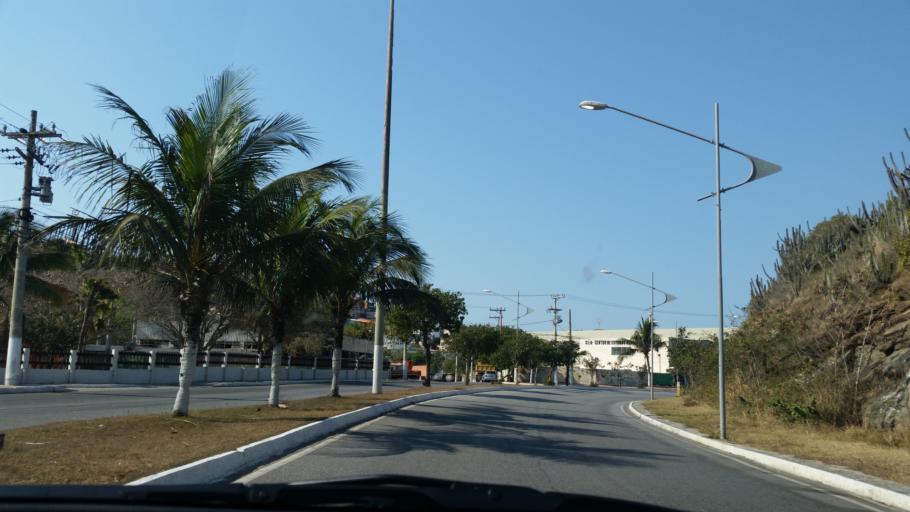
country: BR
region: Rio de Janeiro
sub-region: Arraial Do Cabo
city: Arraial do Cabo
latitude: -22.9630
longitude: -42.0271
